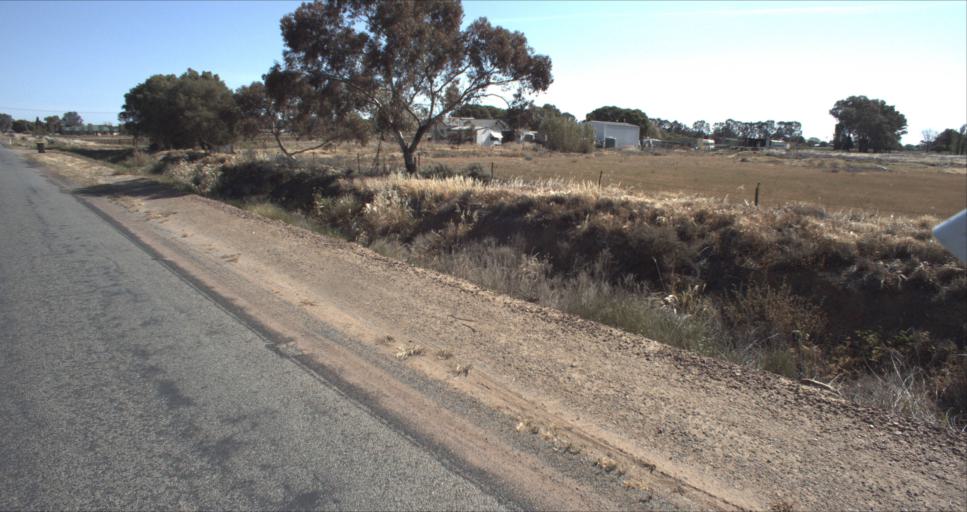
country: AU
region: New South Wales
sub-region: Leeton
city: Leeton
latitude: -34.5379
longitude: 146.4196
